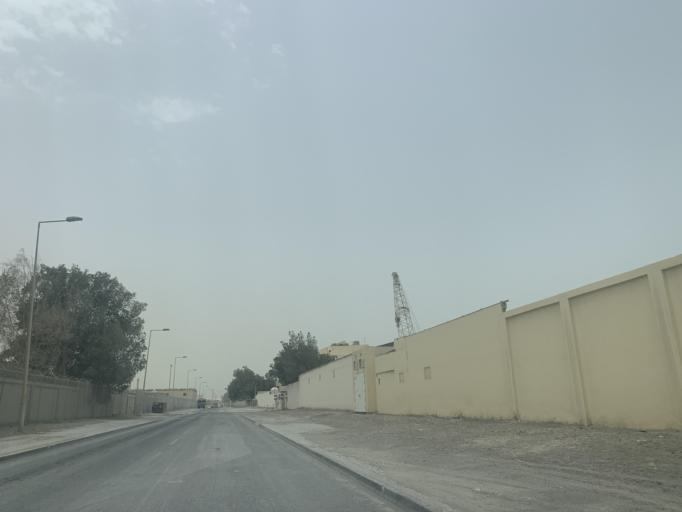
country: BH
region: Northern
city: Sitrah
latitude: 26.1852
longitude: 50.6189
